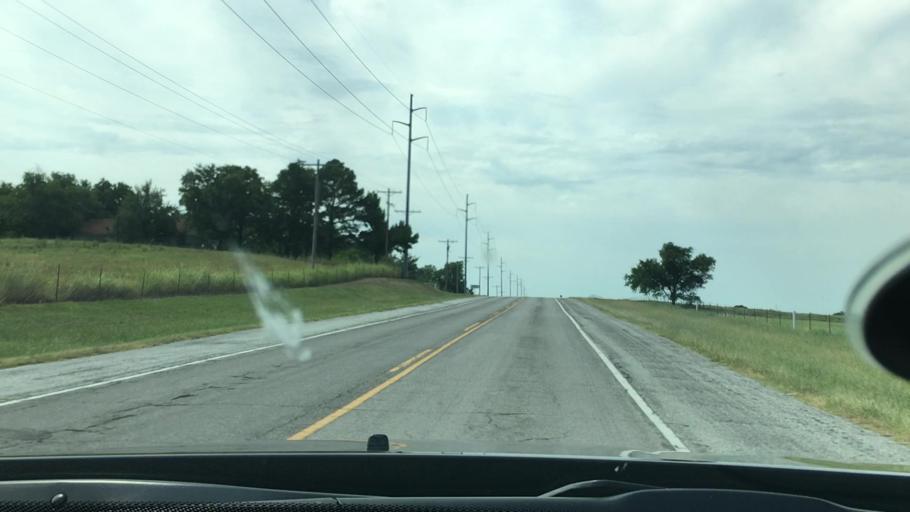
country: US
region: Oklahoma
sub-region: Carter County
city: Ardmore
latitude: 34.3271
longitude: -97.1430
